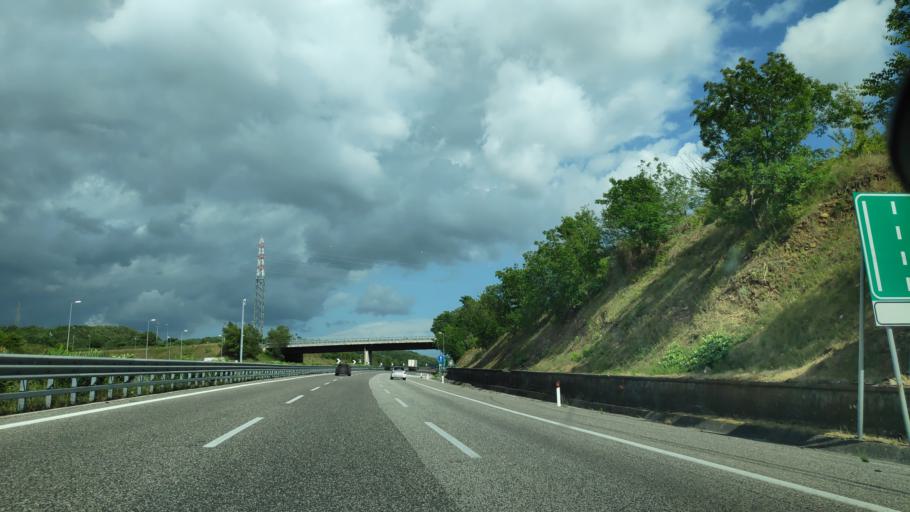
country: IT
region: Campania
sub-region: Provincia di Salerno
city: Contursi Terme
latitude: 40.6285
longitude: 15.2298
